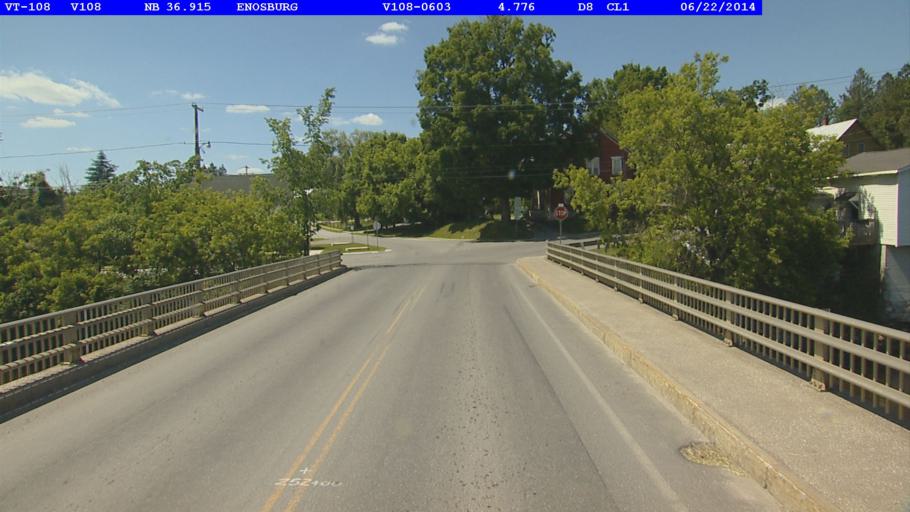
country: US
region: Vermont
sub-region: Franklin County
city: Enosburg Falls
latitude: 44.9027
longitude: -72.8071
